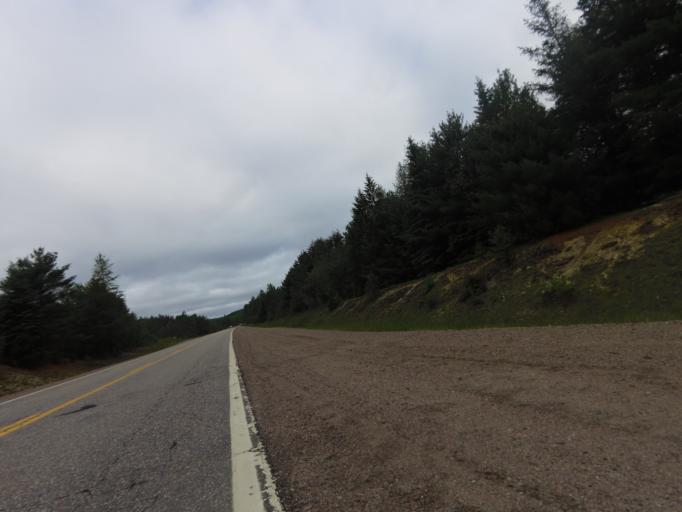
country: CA
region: Quebec
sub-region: Outaouais
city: Shawville
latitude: 45.9069
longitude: -76.3009
